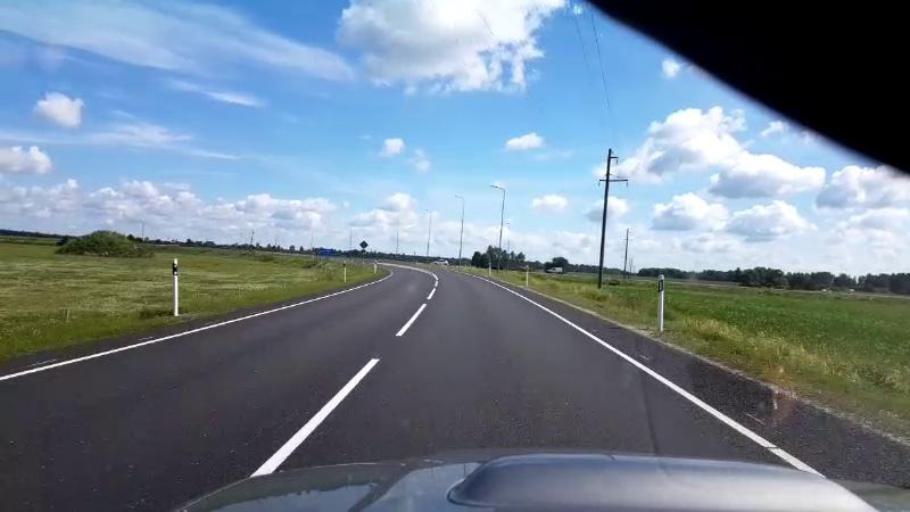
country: EE
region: Jaervamaa
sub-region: Jaerva-Jaani vald
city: Jarva-Jaani
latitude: 59.1389
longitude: 25.7671
